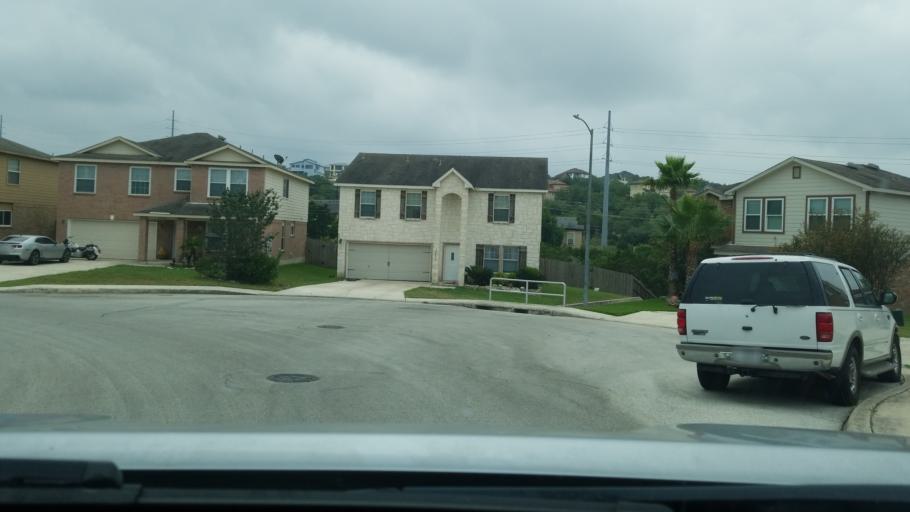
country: US
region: Texas
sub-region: Bexar County
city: Timberwood Park
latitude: 29.6810
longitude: -98.4630
